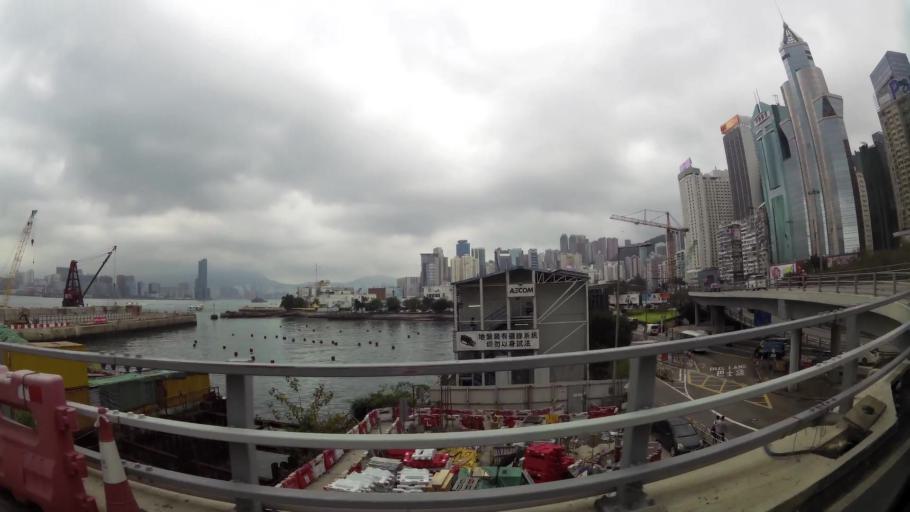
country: HK
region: Wanchai
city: Wan Chai
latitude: 22.2823
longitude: 114.1796
